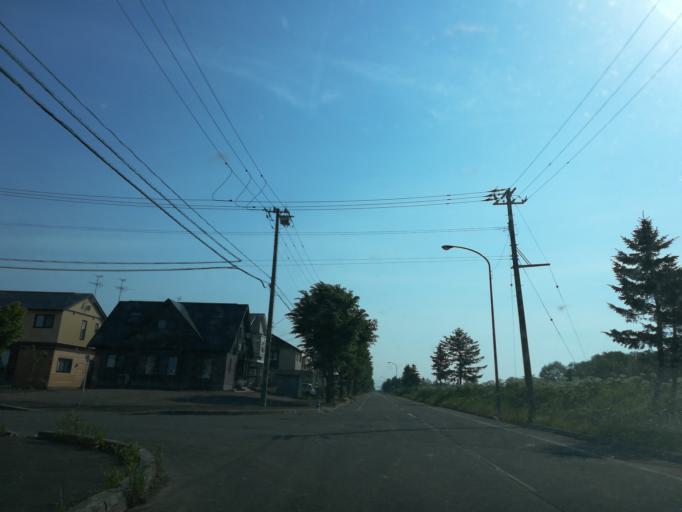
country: JP
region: Hokkaido
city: Iwamizawa
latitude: 43.1705
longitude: 141.7055
